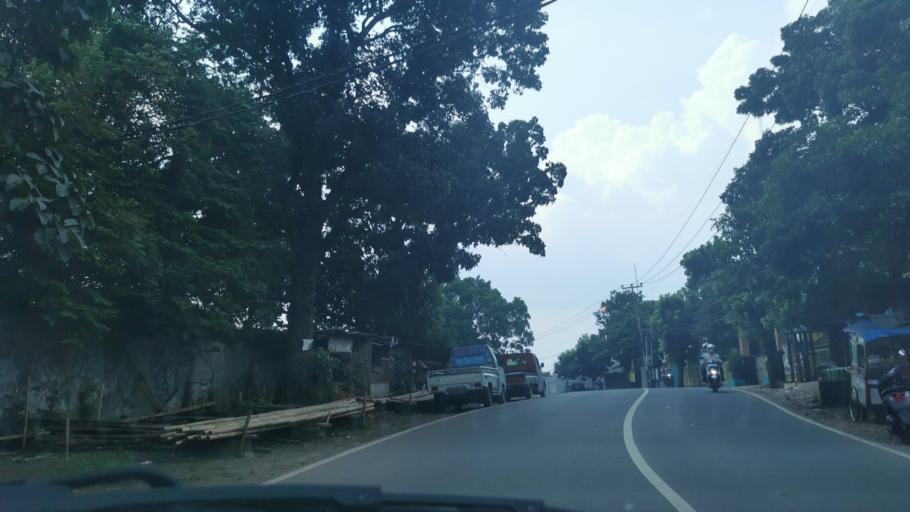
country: ID
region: West Java
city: Depok
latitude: -6.4108
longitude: 106.8313
